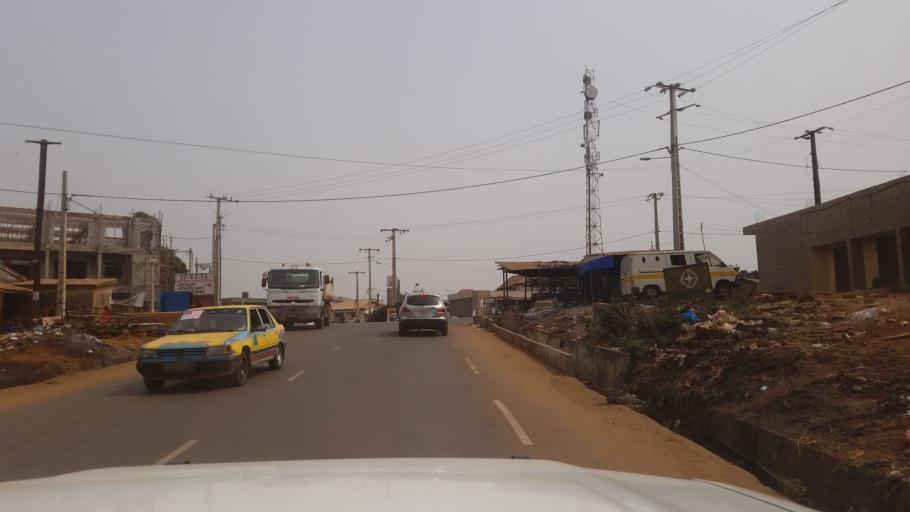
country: GN
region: Kindia
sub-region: Prefecture de Dubreka
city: Dubreka
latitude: 9.6637
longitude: -13.5934
